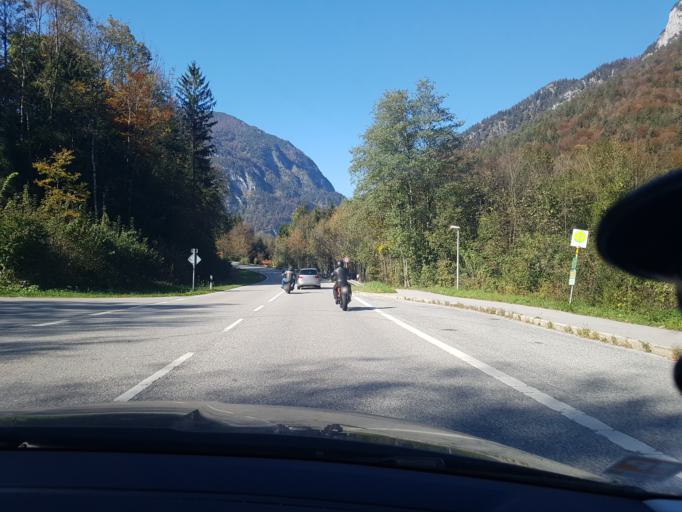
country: DE
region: Bavaria
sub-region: Upper Bavaria
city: Schneizlreuth
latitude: 47.6791
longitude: 12.8267
